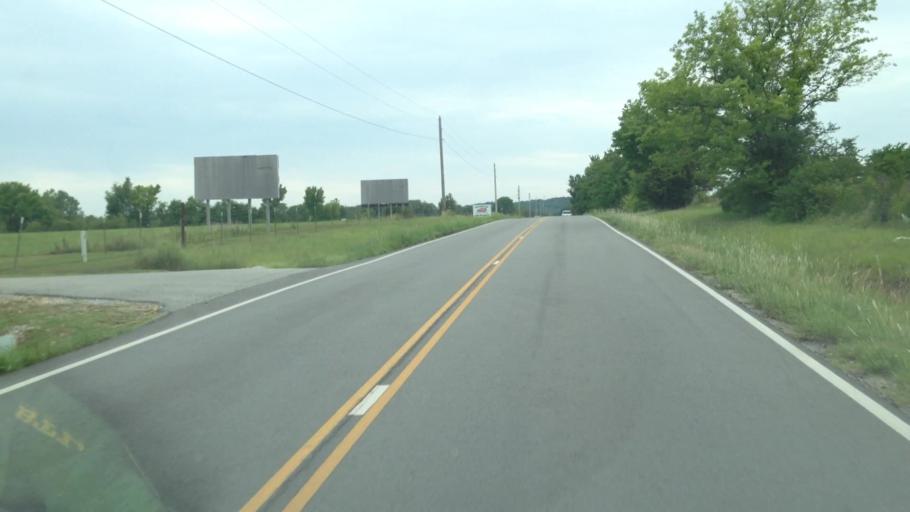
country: US
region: Oklahoma
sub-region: Delaware County
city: Cleora
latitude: 36.5682
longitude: -94.9802
